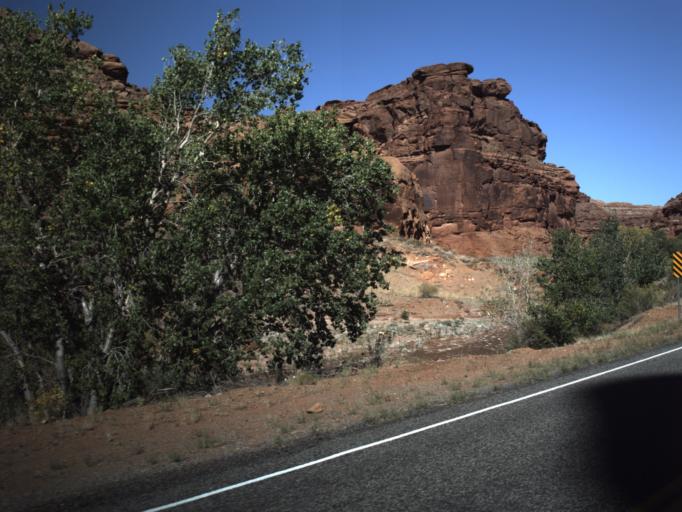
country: US
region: Utah
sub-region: San Juan County
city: Blanding
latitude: 37.9899
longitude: -110.4952
